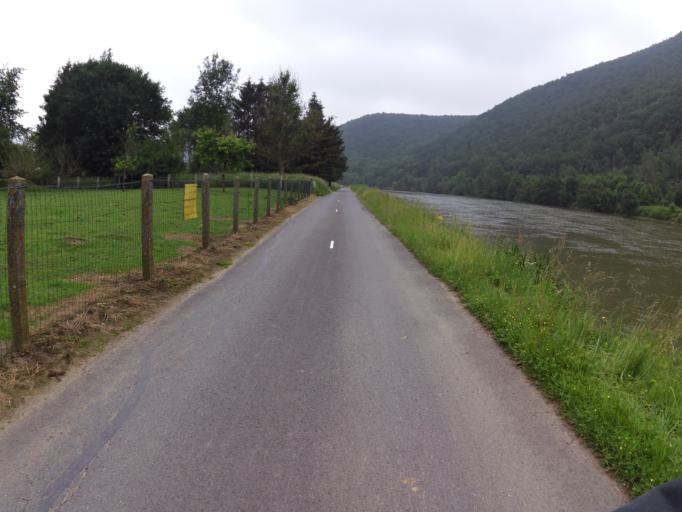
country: FR
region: Champagne-Ardenne
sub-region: Departement des Ardennes
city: Fumay
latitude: 49.9889
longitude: 4.7147
